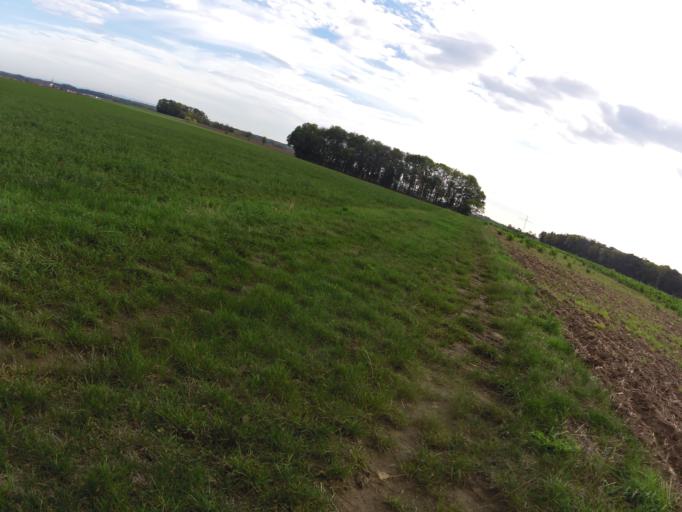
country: DE
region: Bavaria
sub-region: Regierungsbezirk Unterfranken
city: Biebelried
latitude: 49.7346
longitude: 10.0687
